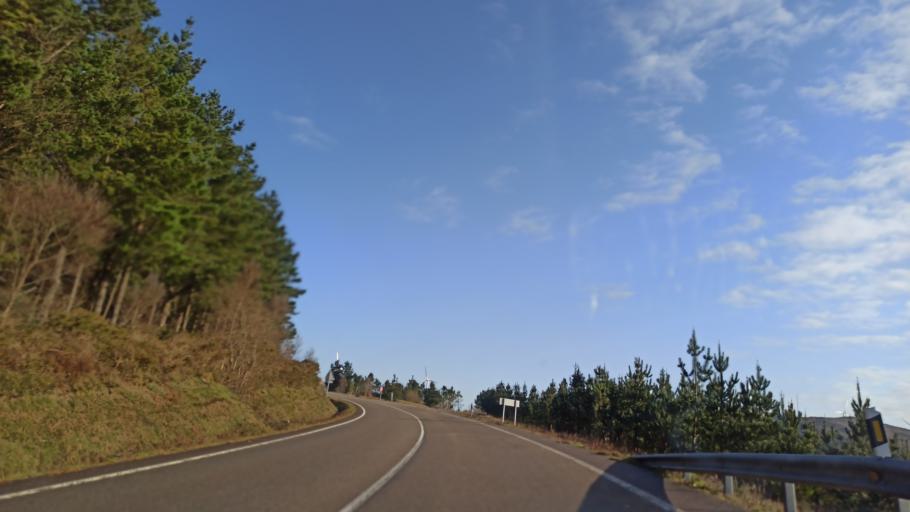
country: ES
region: Galicia
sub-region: Provincia da Coruna
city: As Pontes de Garcia Rodriguez
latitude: 43.5027
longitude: -7.8223
